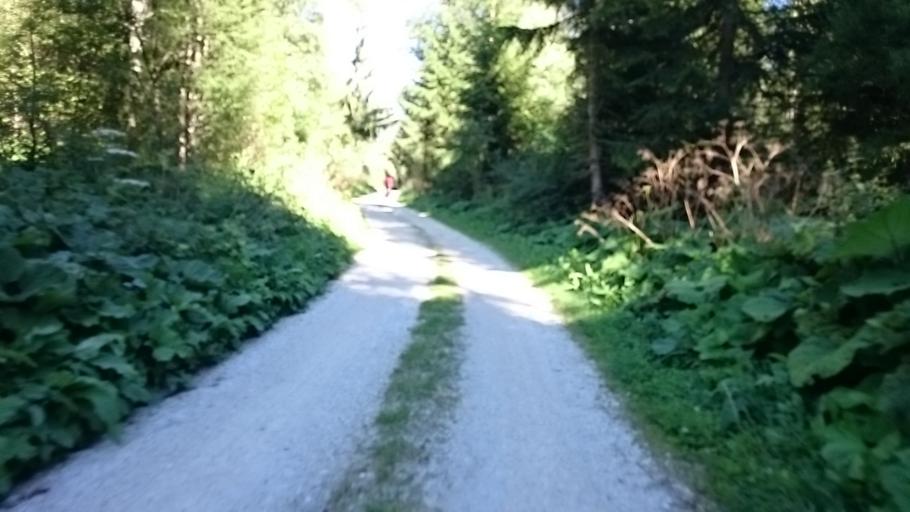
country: IT
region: Trentino-Alto Adige
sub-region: Bolzano
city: Monguelfo
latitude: 46.7604
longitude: 12.0832
